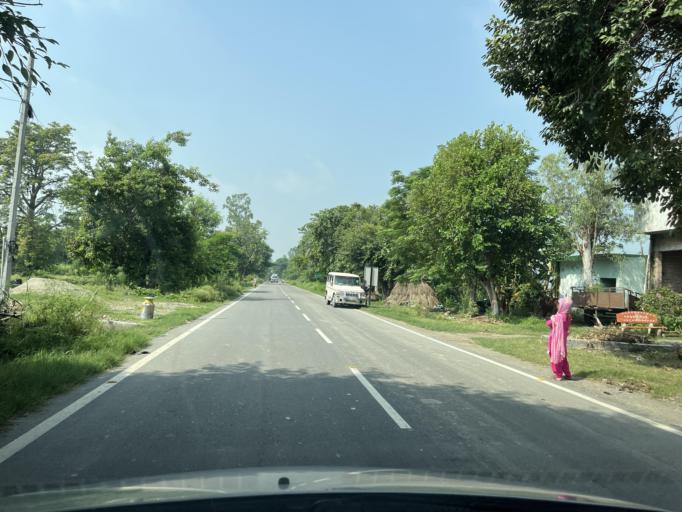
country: IN
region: Uttarakhand
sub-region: Udham Singh Nagar
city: Bazpur
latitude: 29.1817
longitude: 79.1798
